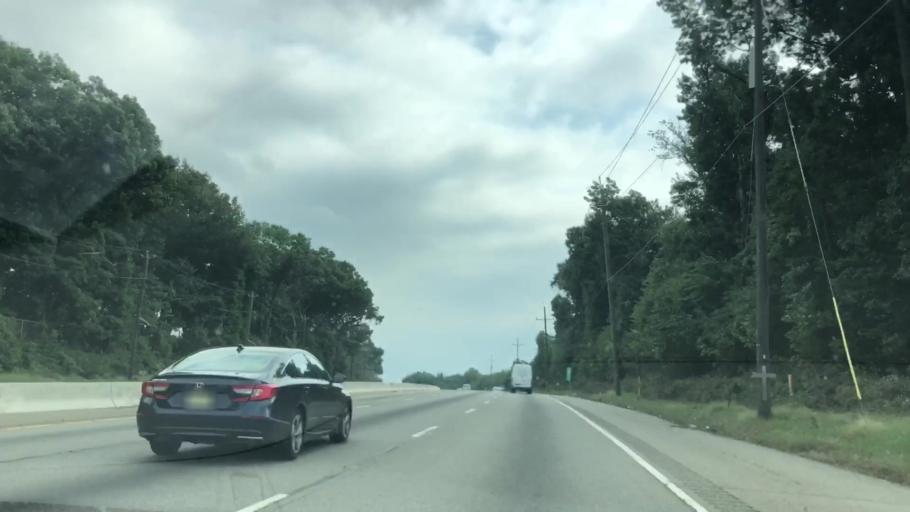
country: US
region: New Jersey
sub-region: Passaic County
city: Clifton
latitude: 40.8446
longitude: -74.1683
